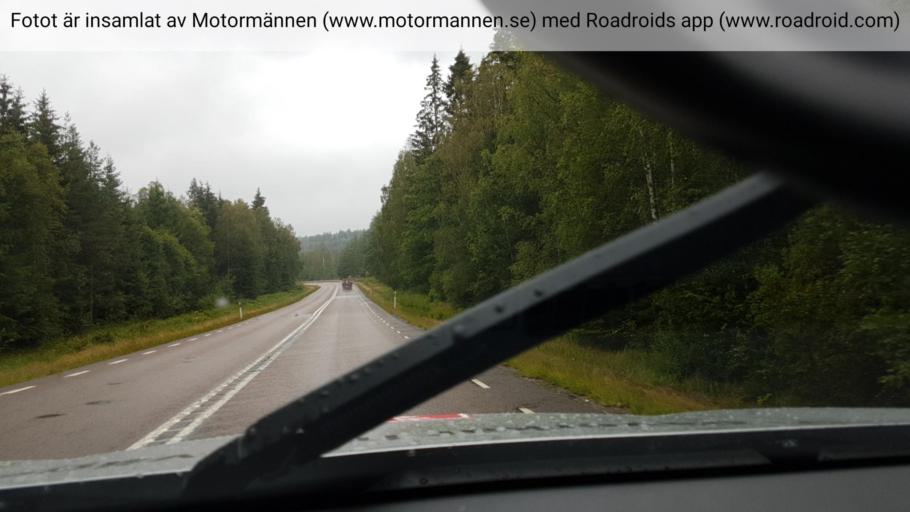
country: SE
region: Vaestra Goetaland
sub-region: Amals Kommun
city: Amal
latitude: 59.0585
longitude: 12.5293
